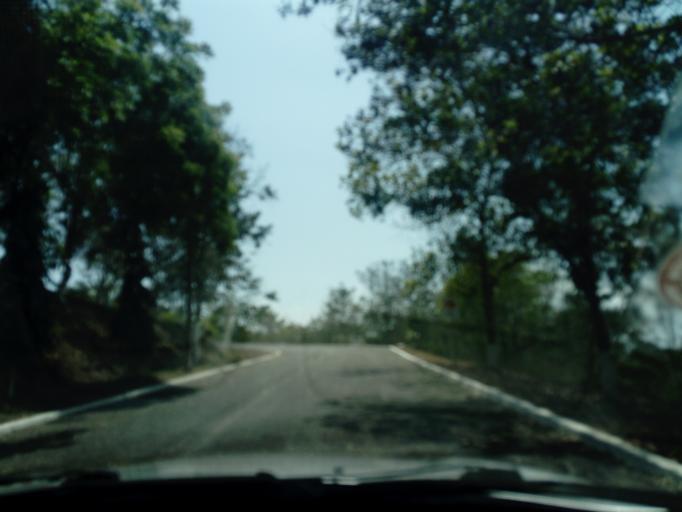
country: GH
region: Central
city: Cape Coast
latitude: 5.1135
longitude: -1.2858
